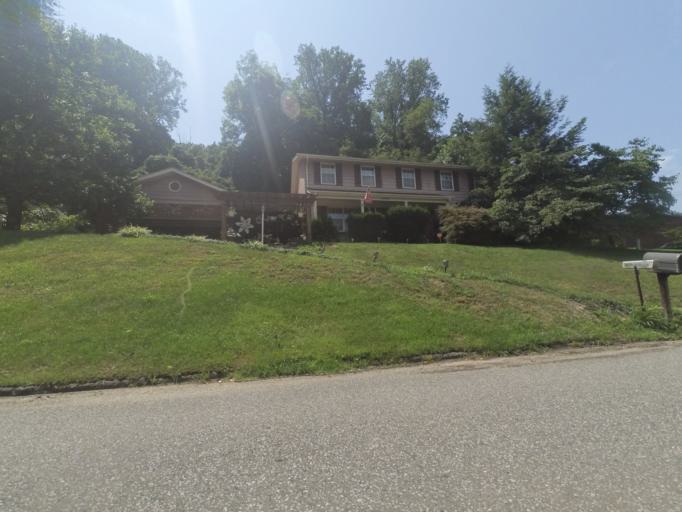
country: US
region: West Virginia
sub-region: Cabell County
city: Huntington
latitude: 38.4012
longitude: -82.4285
